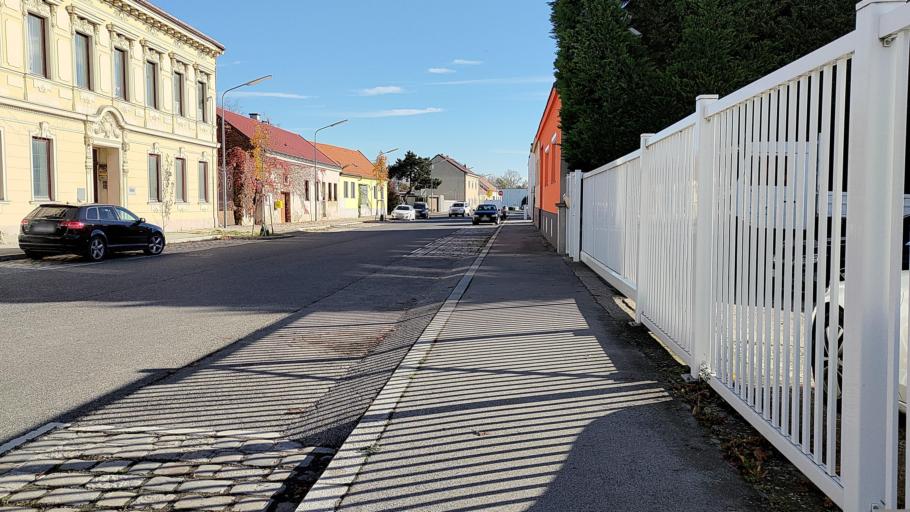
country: AT
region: Lower Austria
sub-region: Politischer Bezirk Wien-Umgebung
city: Schwechat
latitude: 48.1603
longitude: 16.4838
